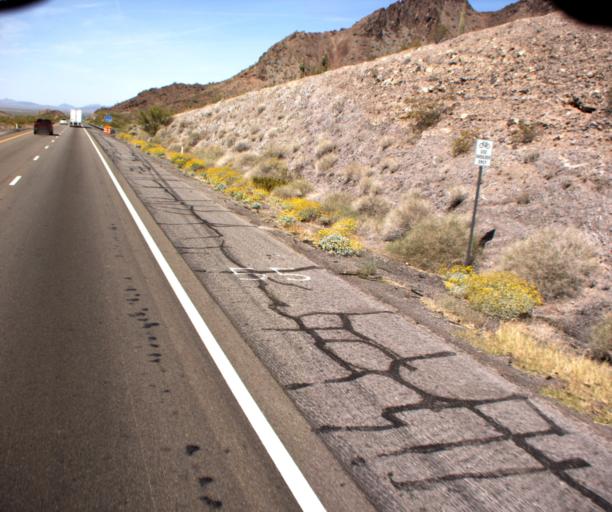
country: US
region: Arizona
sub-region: La Paz County
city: Salome
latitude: 33.6109
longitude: -113.6299
